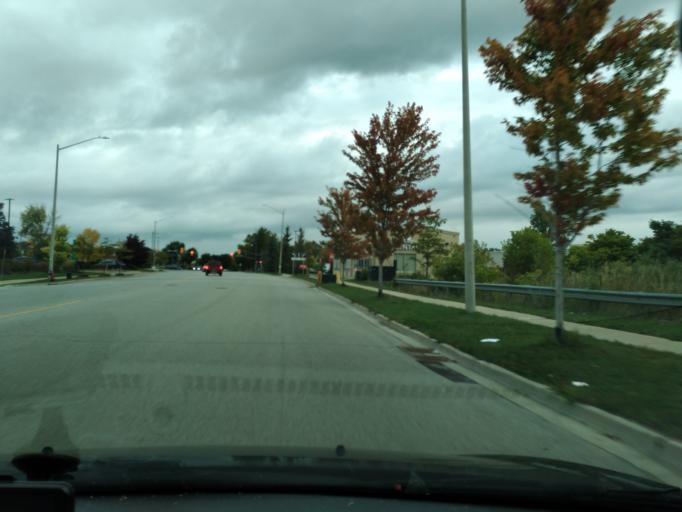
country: CA
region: Ontario
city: Innisfil
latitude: 44.3110
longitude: -79.5582
